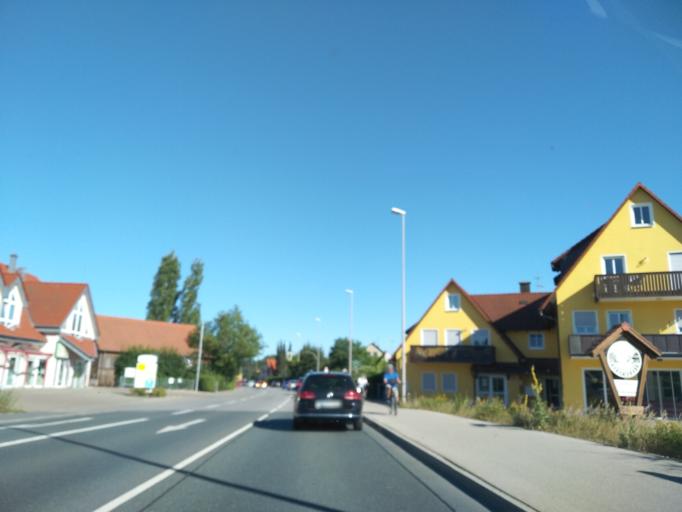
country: DE
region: Bavaria
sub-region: Regierungsbezirk Mittelfranken
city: Hessdorf
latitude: 49.6272
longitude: 10.9365
